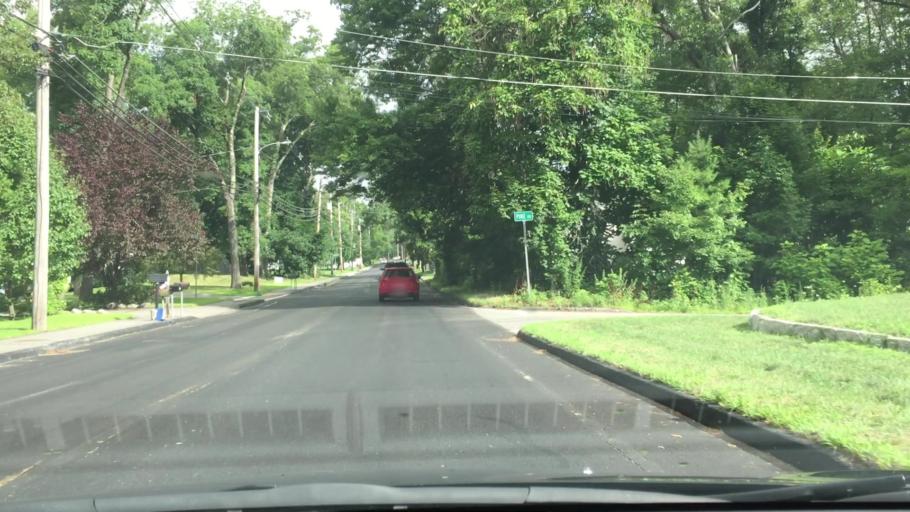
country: US
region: Massachusetts
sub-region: Middlesex County
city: Littleton Common
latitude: 42.5345
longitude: -71.4643
